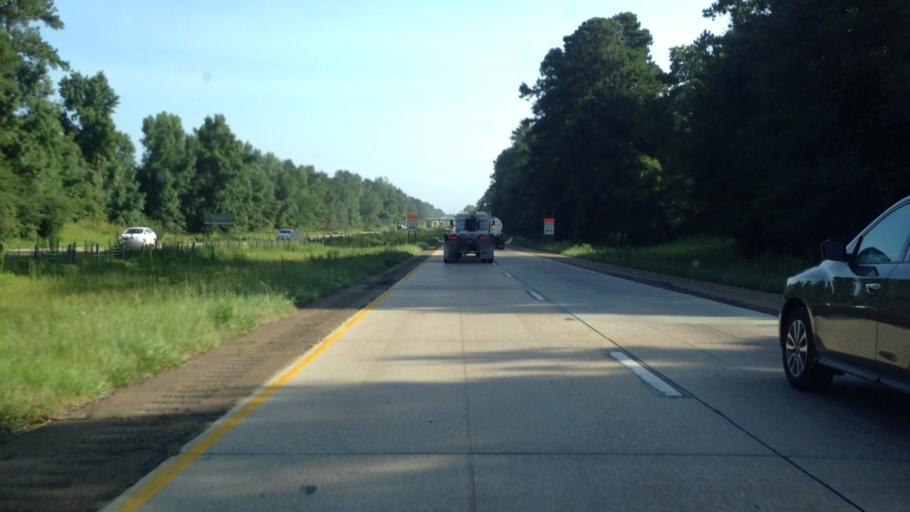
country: US
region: Mississippi
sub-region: Pike County
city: McComb
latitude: 31.2283
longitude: -90.4821
